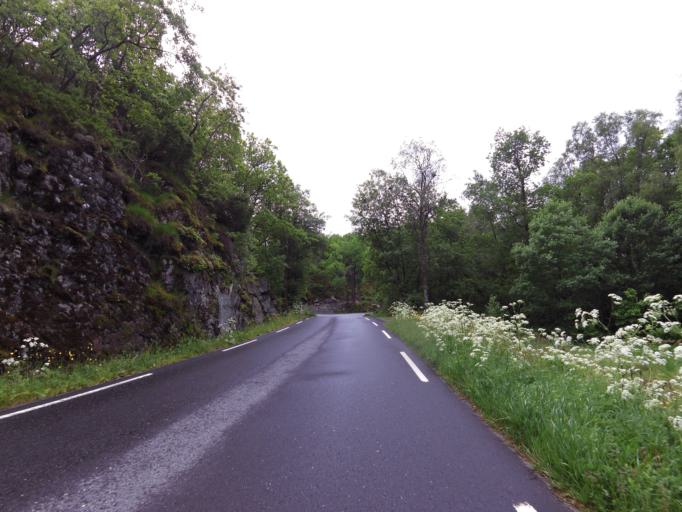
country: NO
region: Vest-Agder
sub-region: Lyngdal
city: Lyngdal
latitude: 58.1002
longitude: 6.9613
